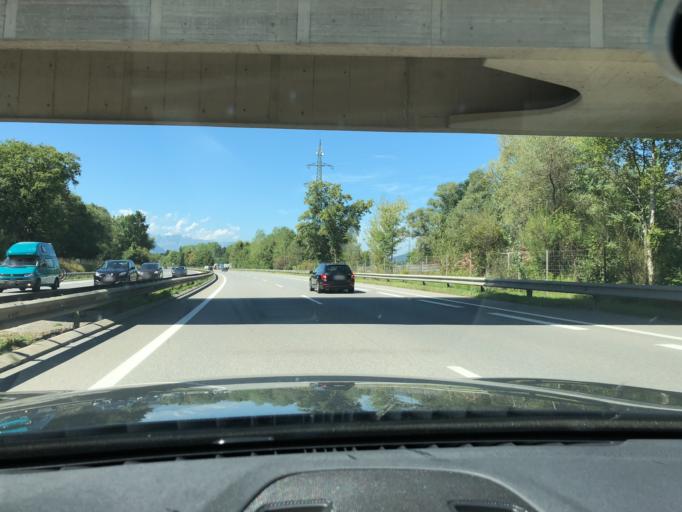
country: AT
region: Vorarlberg
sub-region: Politischer Bezirk Bludenz
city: Nuziders
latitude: 47.1717
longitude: 9.7807
